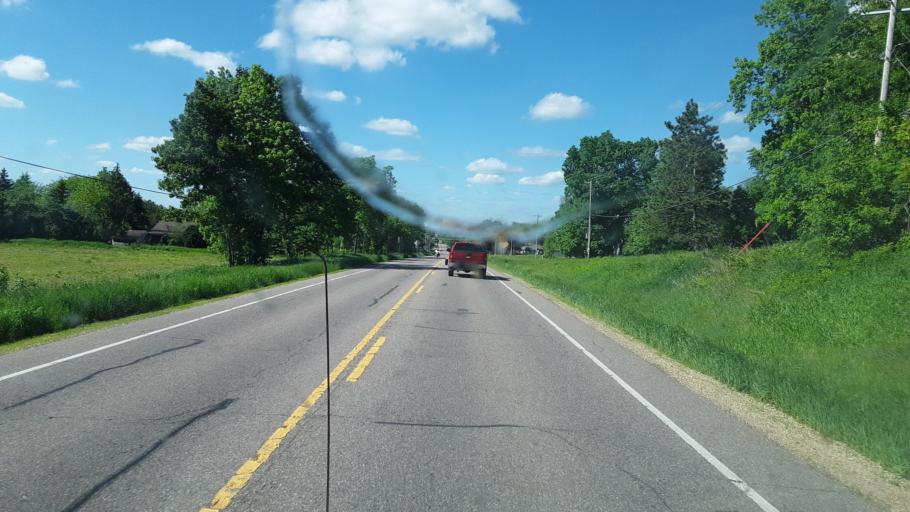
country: US
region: Wisconsin
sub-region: Juneau County
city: Mauston
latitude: 43.7769
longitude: -90.0770
